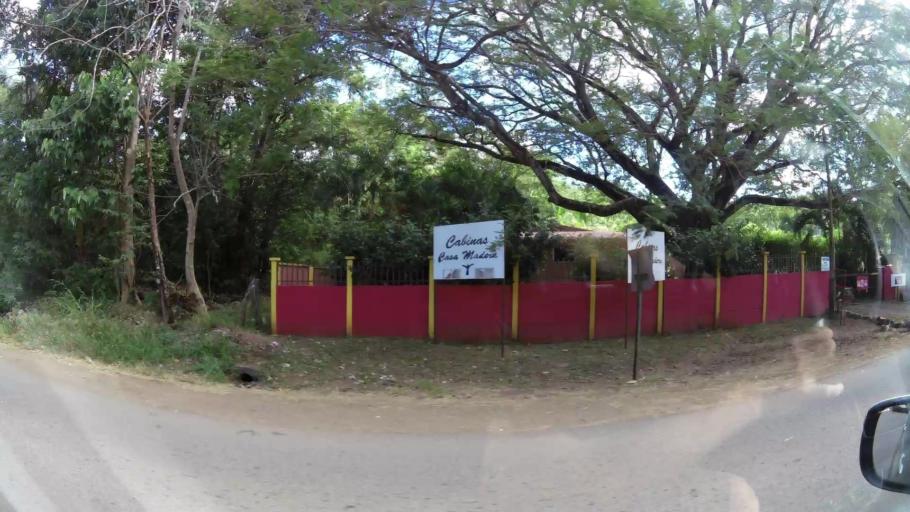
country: CR
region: Guanacaste
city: Santa Cruz
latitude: 10.3078
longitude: -85.8064
